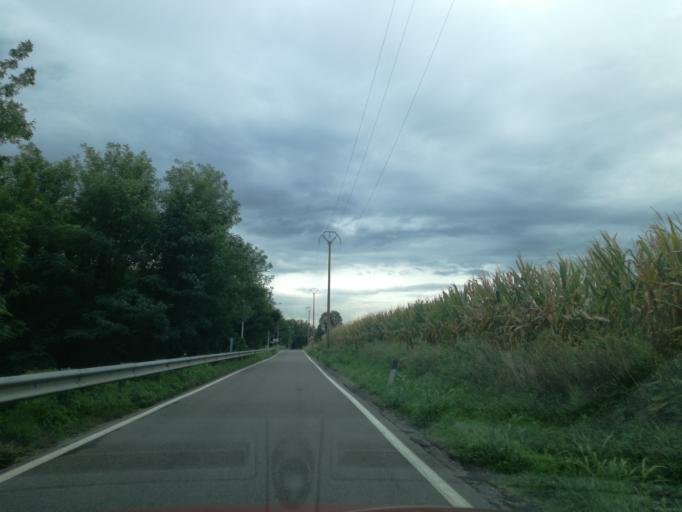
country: IT
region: Lombardy
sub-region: Provincia di Monza e Brianza
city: Cornate d'Adda
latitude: 45.6432
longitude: 9.4621
